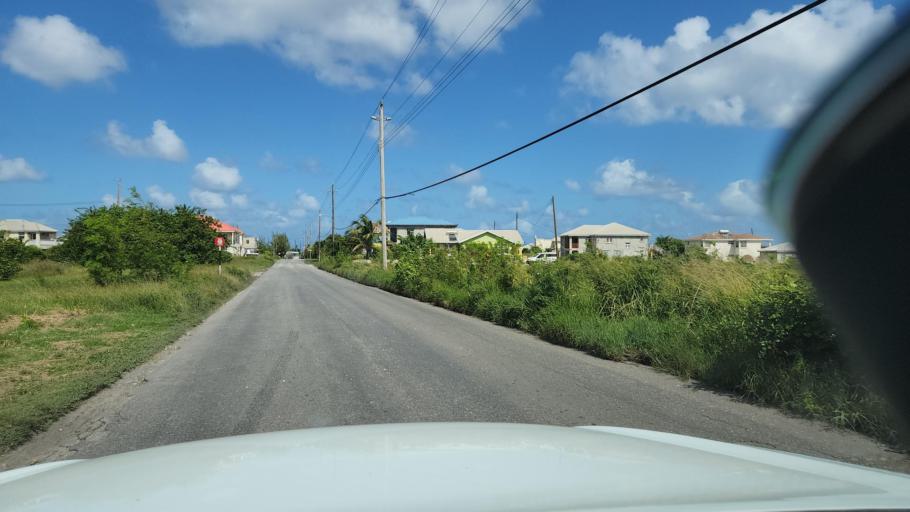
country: BB
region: Saint Philip
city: Crane
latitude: 13.1417
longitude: -59.4313
